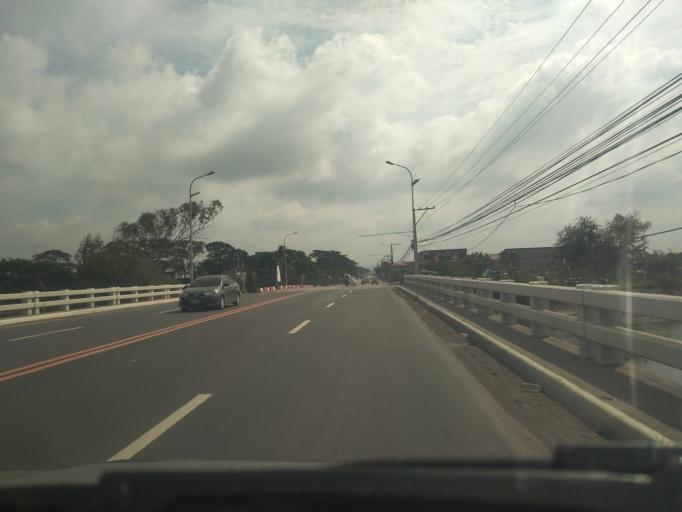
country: PH
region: Central Luzon
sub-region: Province of Pampanga
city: Pau
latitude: 15.0048
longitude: 120.7186
